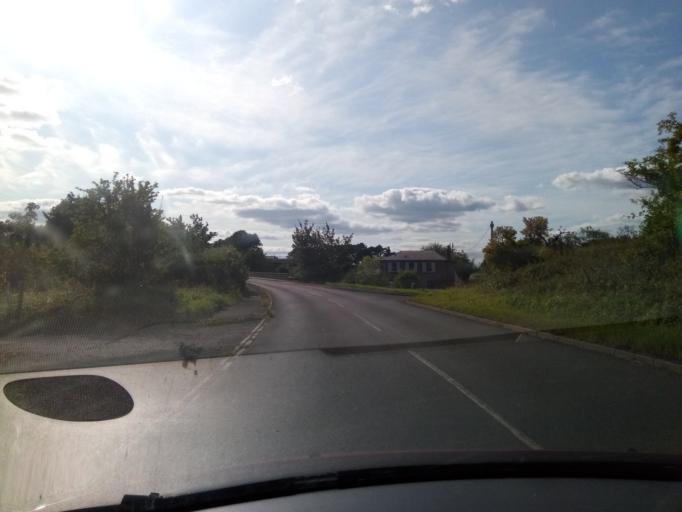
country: GB
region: England
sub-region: Northumberland
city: Berwick-Upon-Tweed
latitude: 55.7668
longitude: -2.0681
